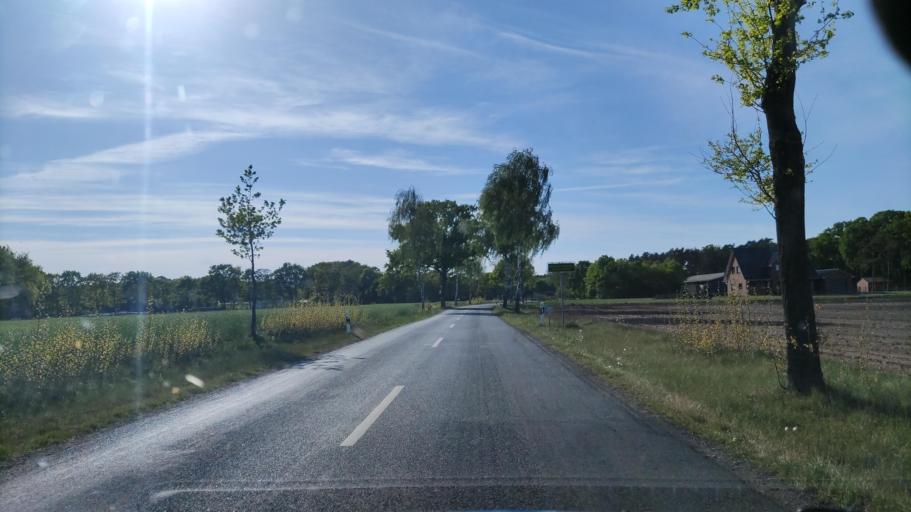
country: DE
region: Lower Saxony
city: Schneverdingen
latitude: 53.1749
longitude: 9.8026
